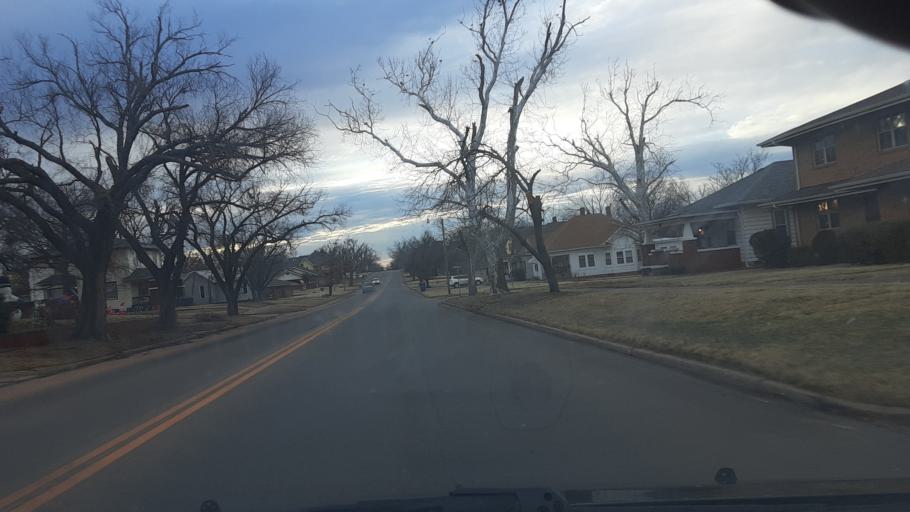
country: US
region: Oklahoma
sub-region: Logan County
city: Guthrie
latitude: 35.8802
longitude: -97.4131
